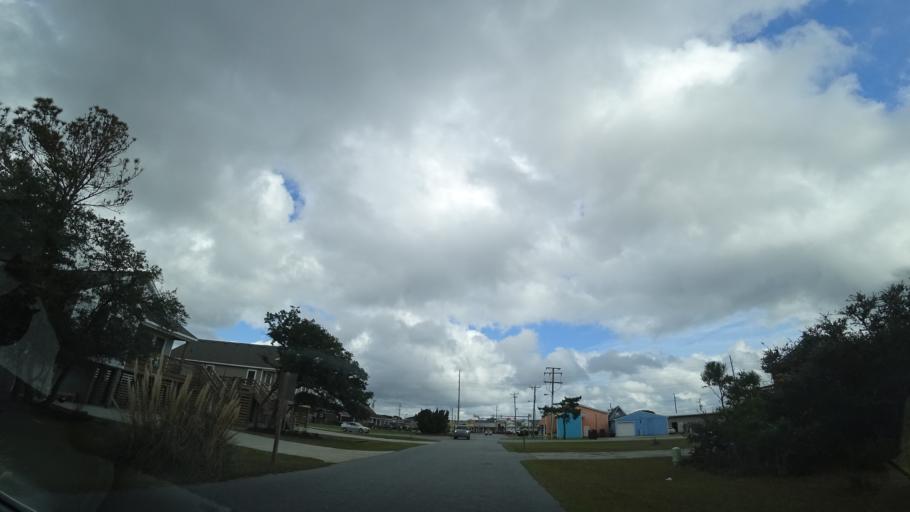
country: US
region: North Carolina
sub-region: Dare County
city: Kill Devil Hills
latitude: 35.9971
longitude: -75.6528
